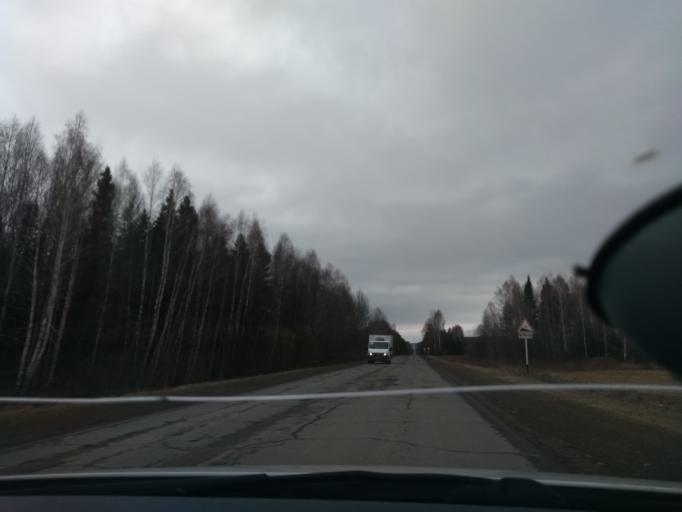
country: RU
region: Perm
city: Kungur
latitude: 57.3649
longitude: 56.8238
